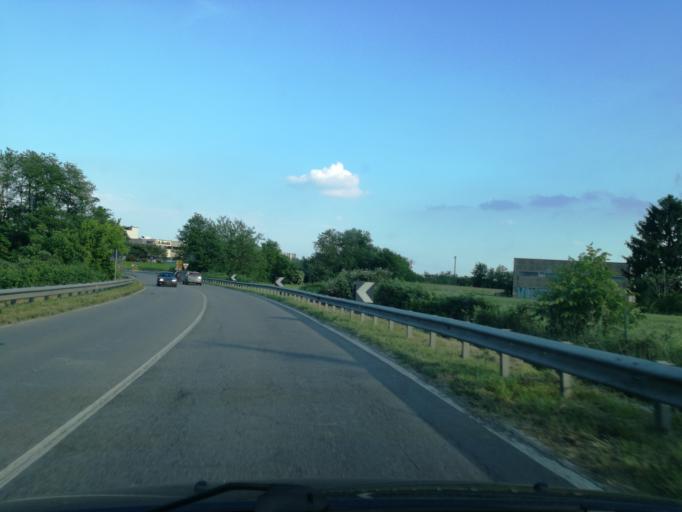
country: IT
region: Lombardy
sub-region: Provincia di Monza e Brianza
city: Cornate d'Adda
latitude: 45.6257
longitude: 9.4650
